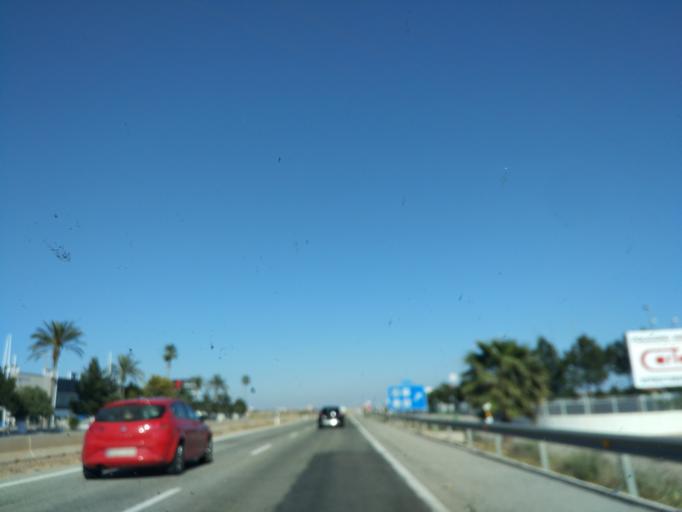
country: ES
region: Murcia
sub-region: Murcia
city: Murcia
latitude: 37.8668
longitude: -1.1139
